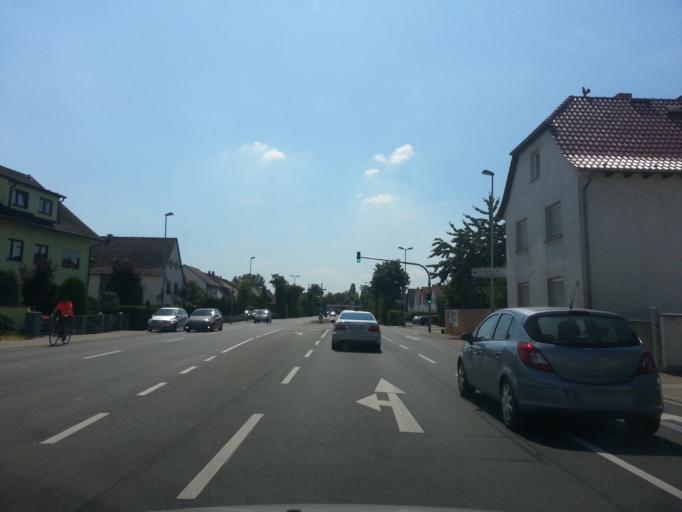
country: DE
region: Hesse
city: Lampertheim
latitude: 49.5944
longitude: 8.4619
